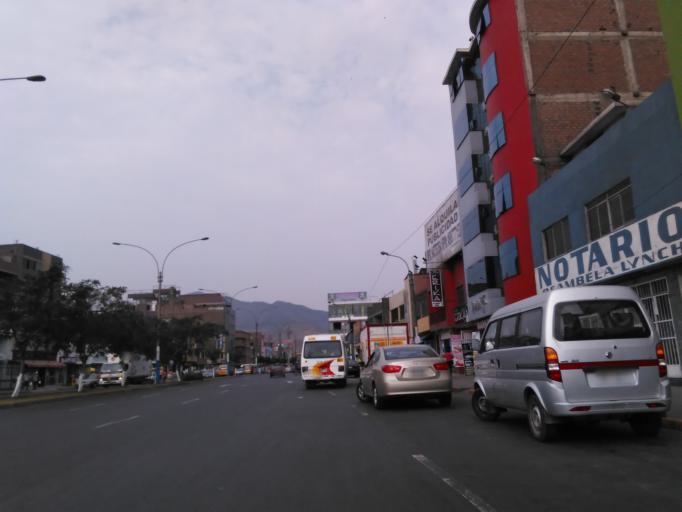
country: PE
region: Lima
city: Lima
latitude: -12.0281
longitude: -77.0568
